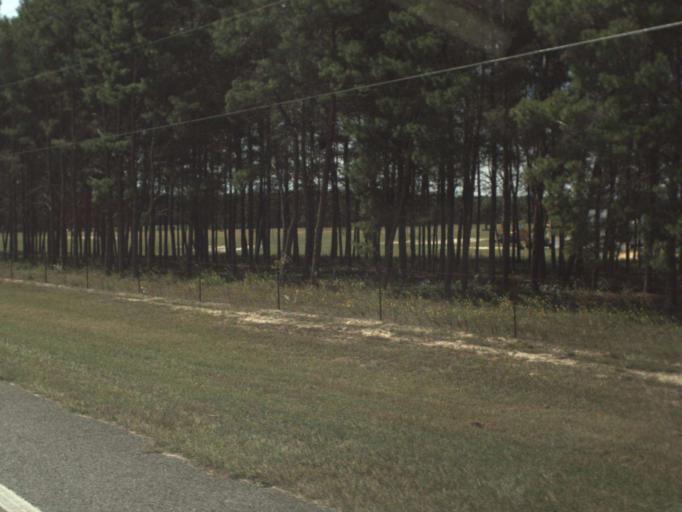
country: US
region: Florida
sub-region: Bay County
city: Youngstown
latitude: 30.5170
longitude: -85.6541
